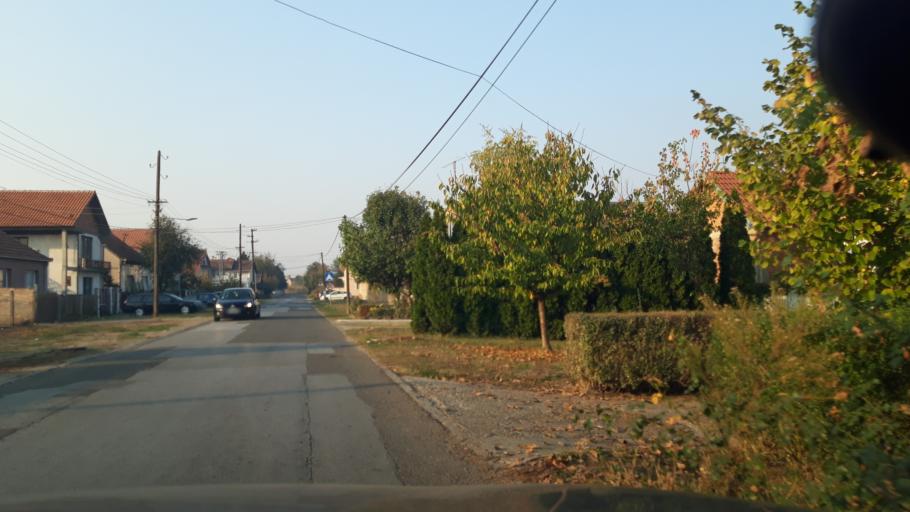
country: RS
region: Autonomna Pokrajina Vojvodina
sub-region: Sremski Okrug
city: Stara Pazova
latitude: 44.9954
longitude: 20.1453
